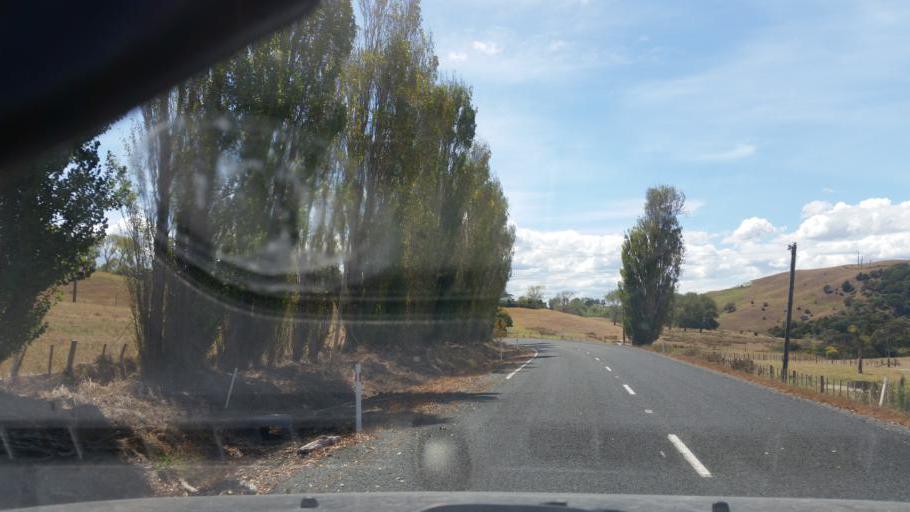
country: NZ
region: Northland
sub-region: Kaipara District
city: Dargaville
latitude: -36.1658
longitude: 174.1664
